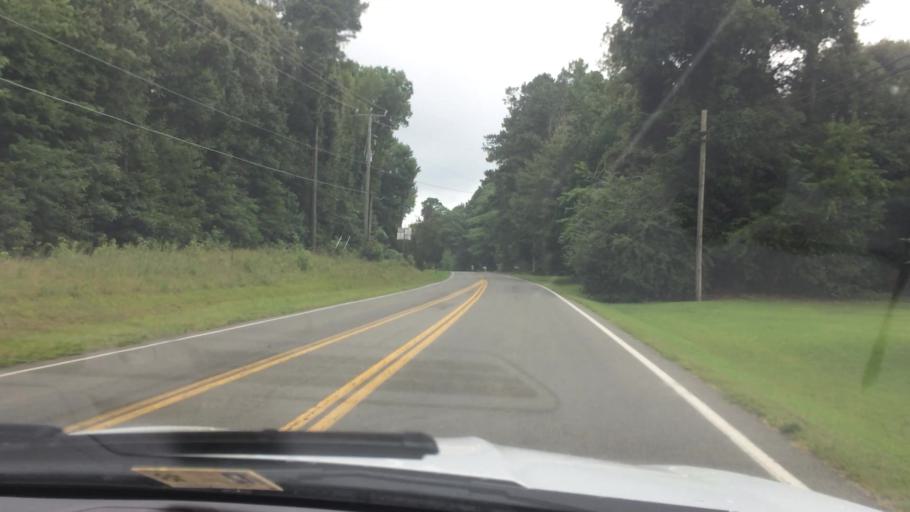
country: US
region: Virginia
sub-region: Charles City County
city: Charles City
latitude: 37.4120
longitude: -77.0453
